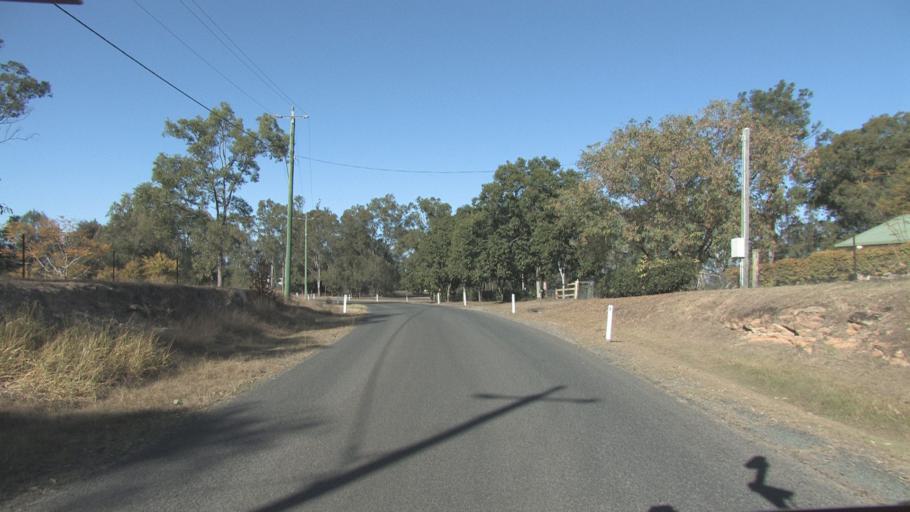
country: AU
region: Queensland
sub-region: Logan
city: North Maclean
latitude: -27.8317
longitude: 152.9895
